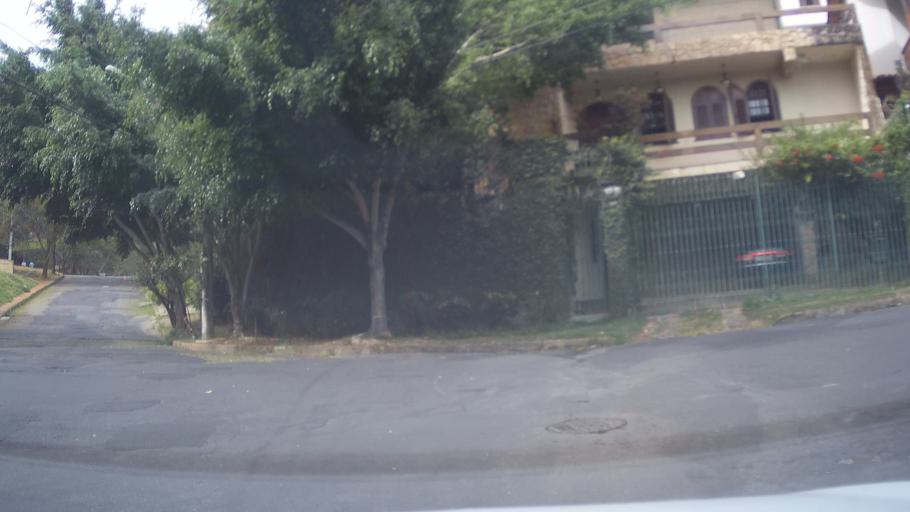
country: BR
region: Minas Gerais
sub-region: Belo Horizonte
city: Belo Horizonte
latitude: -19.9548
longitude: -43.9209
